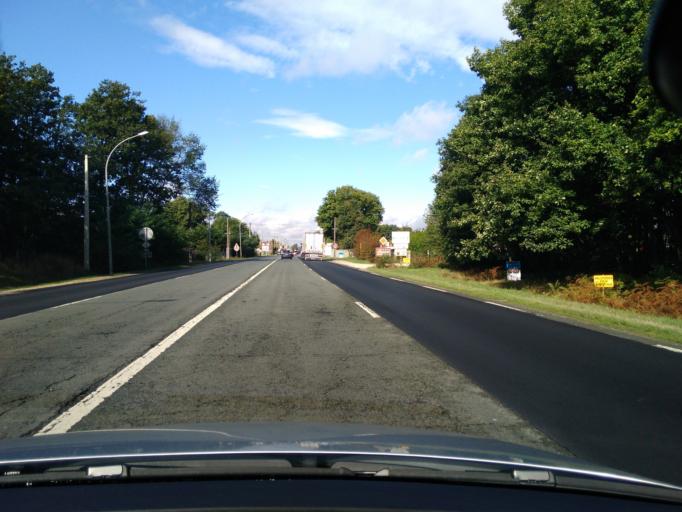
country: FR
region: Centre
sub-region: Departement d'Eure-et-Loir
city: Saint-Remy-sur-Avre
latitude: 48.7534
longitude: 1.2558
